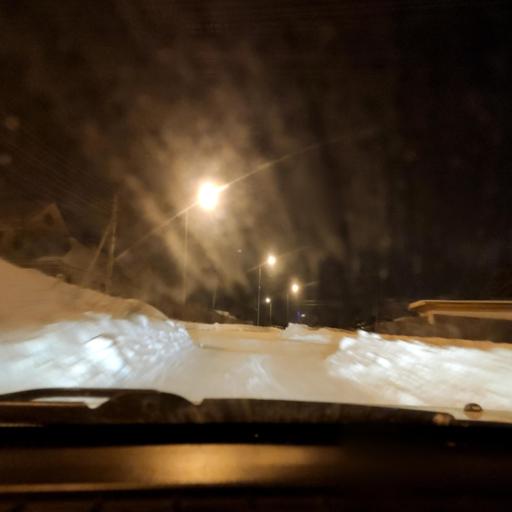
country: RU
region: Perm
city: Perm
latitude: 58.0269
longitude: 56.3478
